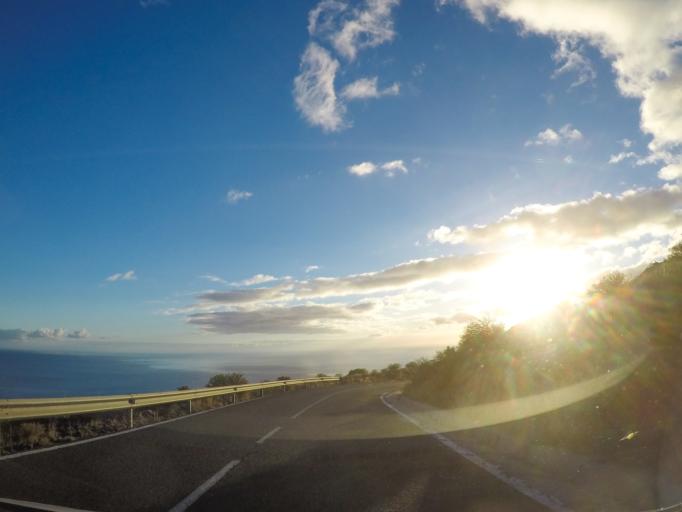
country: ES
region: Canary Islands
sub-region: Provincia de Santa Cruz de Tenerife
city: Alajero
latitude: 28.0406
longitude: -17.2325
